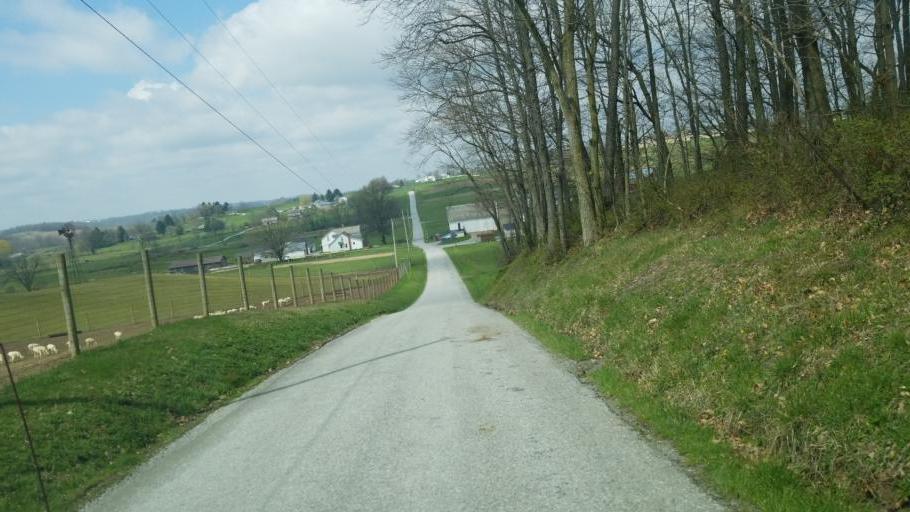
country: US
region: Ohio
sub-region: Holmes County
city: Millersburg
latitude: 40.6131
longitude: -81.8116
